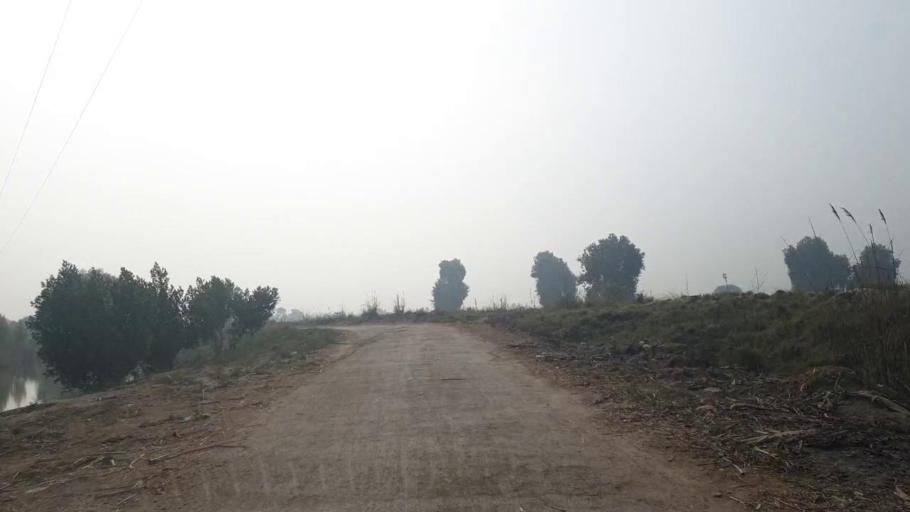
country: PK
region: Sindh
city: Tando Adam
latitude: 25.7665
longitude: 68.6073
